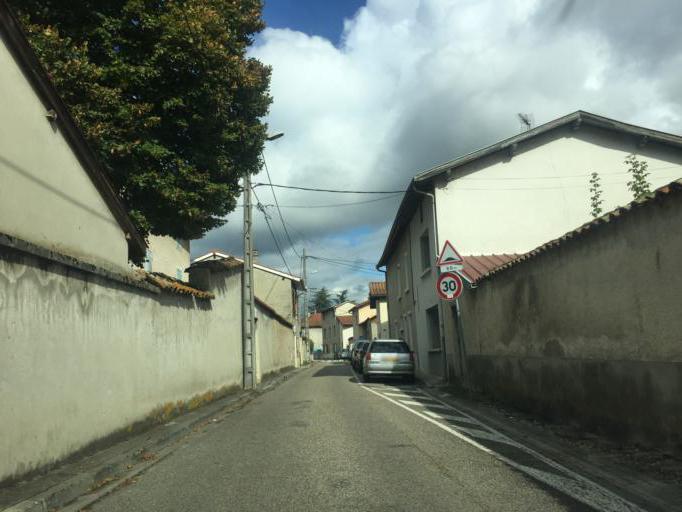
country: FR
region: Rhone-Alpes
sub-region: Departement de l'Ain
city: Dagneux
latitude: 45.8515
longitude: 5.0704
